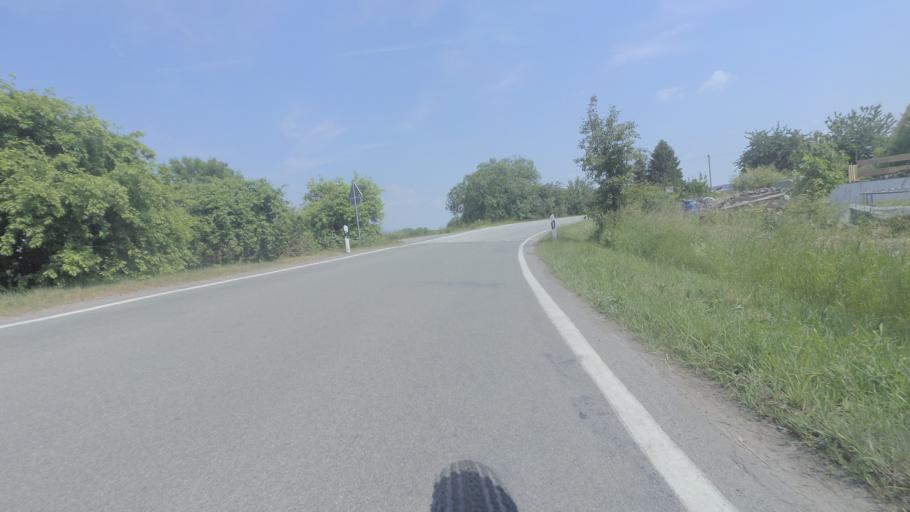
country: DE
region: Saxony-Anhalt
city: Ballenstedt
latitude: 51.7190
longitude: 11.2648
